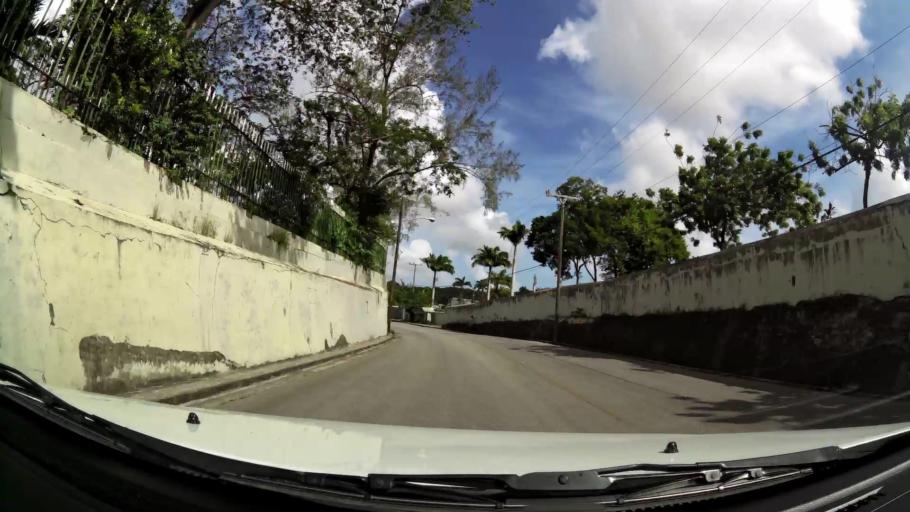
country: BB
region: Saint Michael
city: Bridgetown
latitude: 13.0980
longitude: -59.6090
